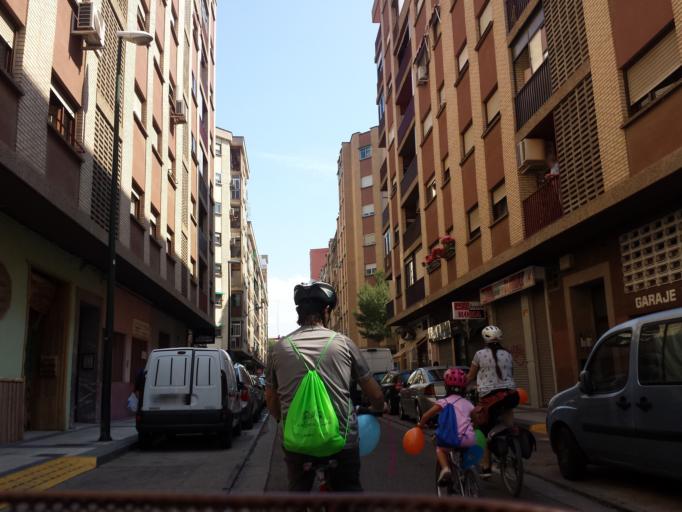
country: ES
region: Aragon
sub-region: Provincia de Zaragoza
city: Almozara
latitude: 41.6610
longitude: -0.8984
